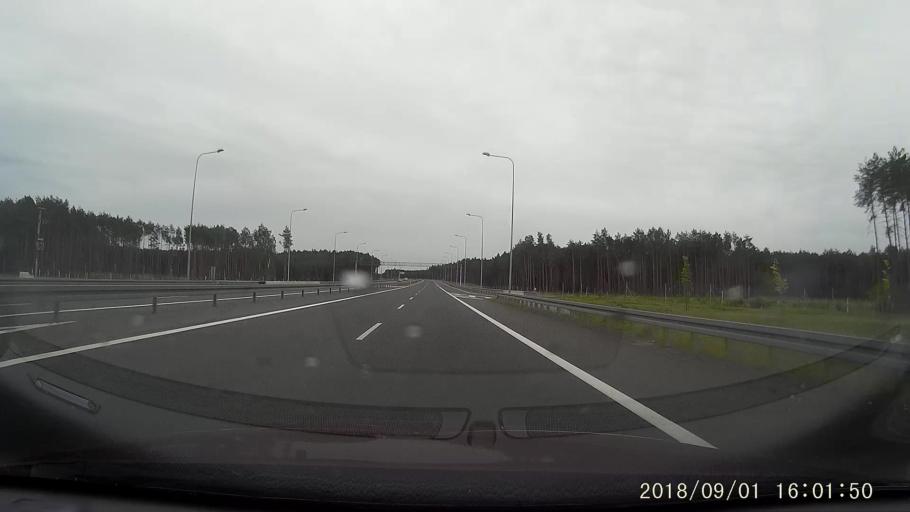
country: PL
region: Lubusz
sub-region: Powiat gorzowski
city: Deszczno
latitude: 52.6238
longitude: 15.3815
